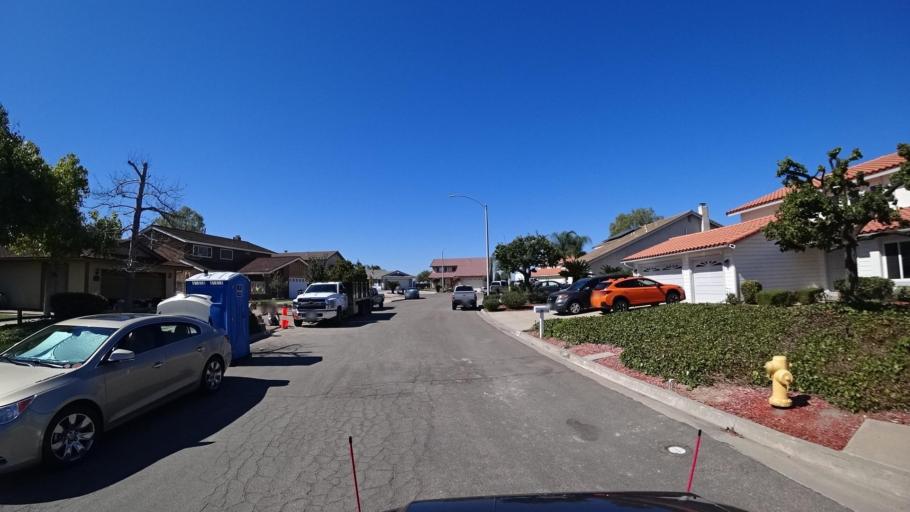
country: US
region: California
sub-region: San Diego County
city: Bonita
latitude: 32.6614
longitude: -116.9971
